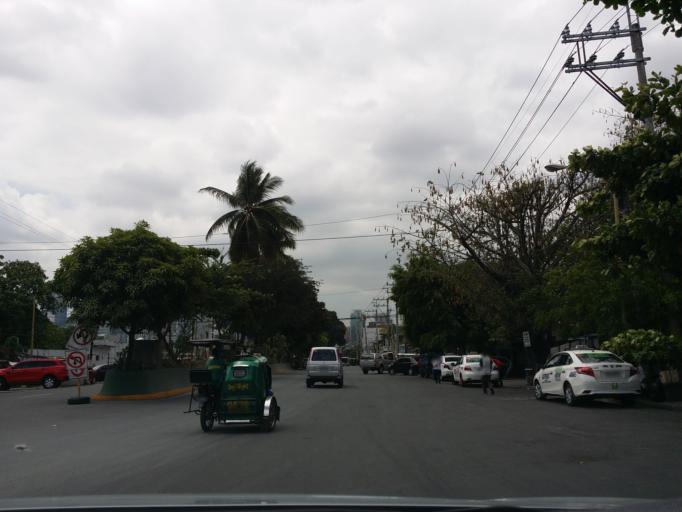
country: PH
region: Metro Manila
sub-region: Mandaluyong
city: Mandaluyong City
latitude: 14.5751
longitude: 121.0165
